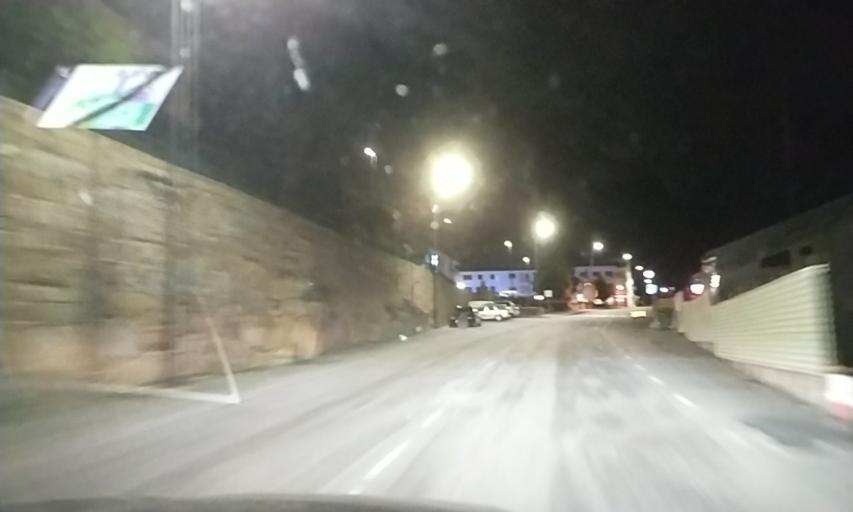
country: PT
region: Braganca
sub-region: Miranda do Douro
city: Miranda do Douro
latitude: 41.4990
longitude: -6.2732
